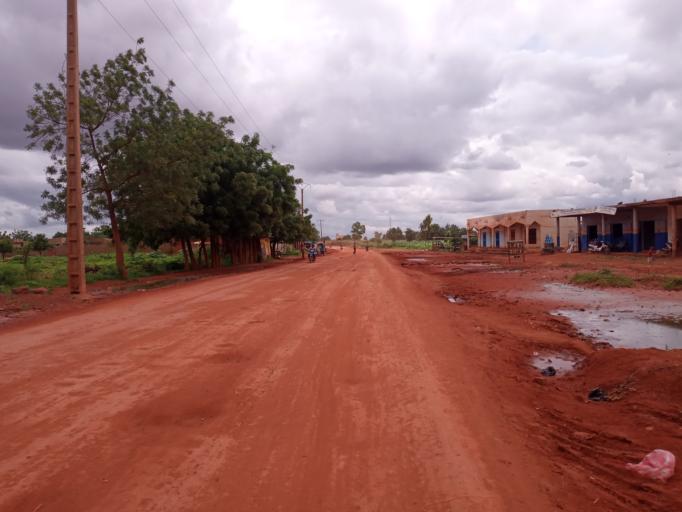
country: ML
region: Bamako
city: Bamako
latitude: 12.5420
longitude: -7.9943
